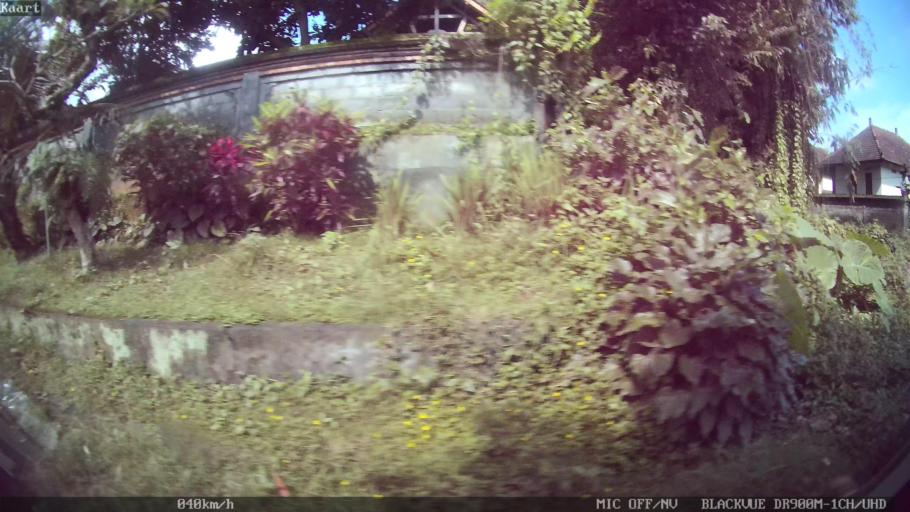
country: ID
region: Bali
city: Banjar Pesalakan
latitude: -8.4989
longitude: 115.2975
